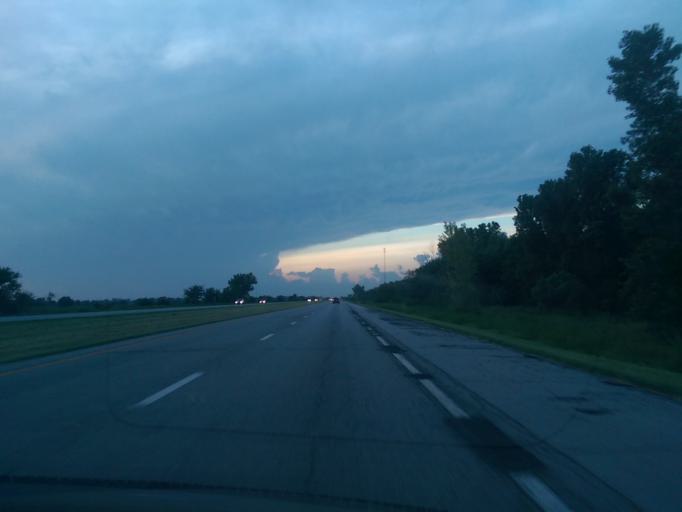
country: US
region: Iowa
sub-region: Fremont County
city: Hamburg
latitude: 40.5331
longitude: -95.6149
